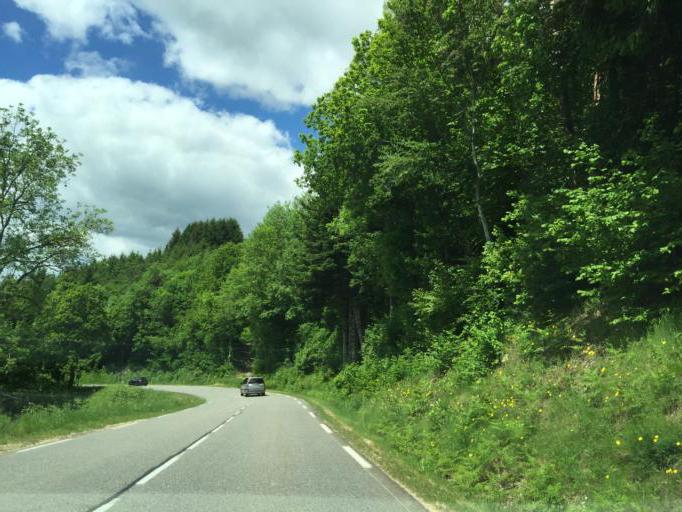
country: FR
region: Auvergne
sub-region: Departement du Puy-de-Dome
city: Ambert
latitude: 45.5301
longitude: 3.8006
